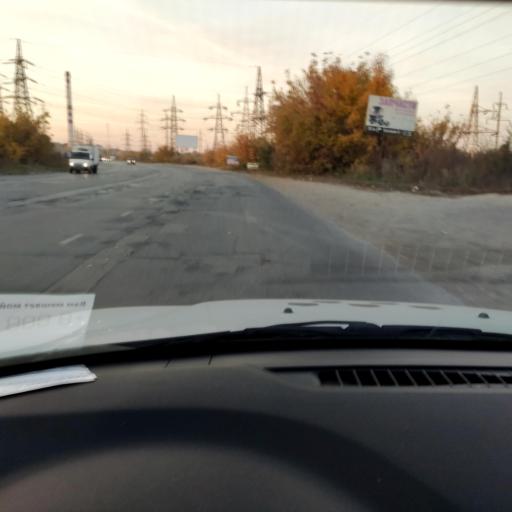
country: RU
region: Samara
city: Tol'yatti
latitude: 53.5202
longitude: 49.4675
